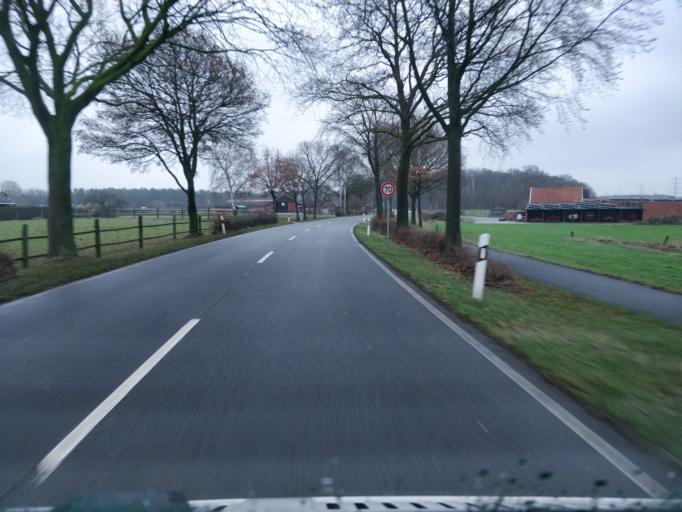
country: DE
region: North Rhine-Westphalia
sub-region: Regierungsbezirk Dusseldorf
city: Mehrhoog
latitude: 51.7582
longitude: 6.5222
